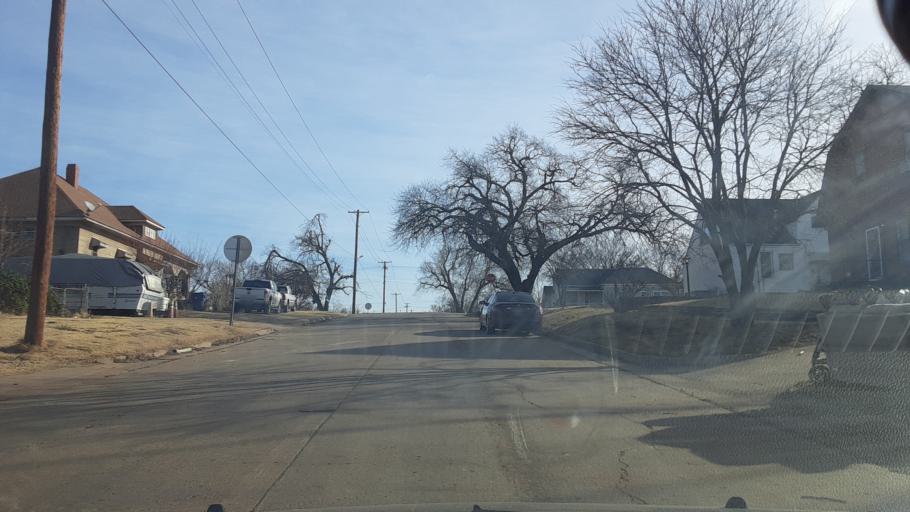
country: US
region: Oklahoma
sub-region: Logan County
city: Guthrie
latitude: 35.8853
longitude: -97.4249
